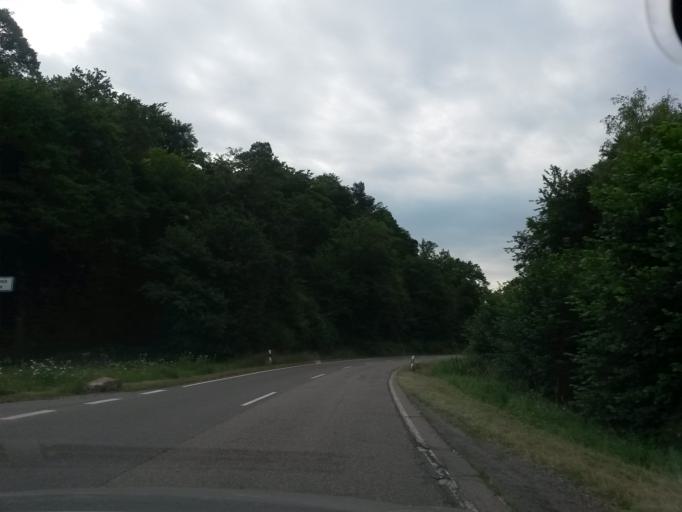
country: DE
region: Baden-Wuerttemberg
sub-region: Karlsruhe Region
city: Ispringen
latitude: 48.8970
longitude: 8.6456
